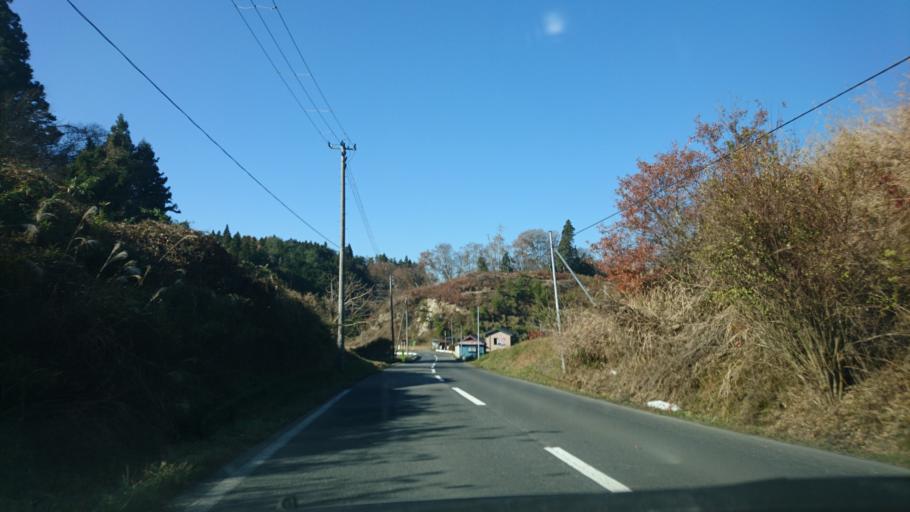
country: JP
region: Iwate
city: Ichinoseki
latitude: 38.9028
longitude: 141.4016
